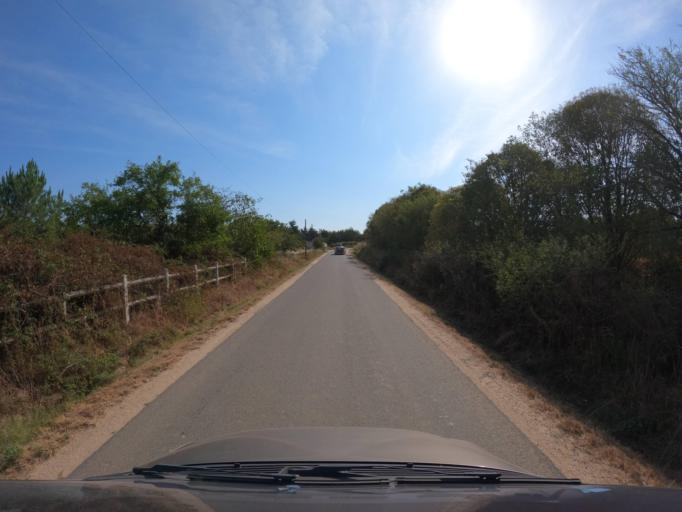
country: FR
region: Pays de la Loire
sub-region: Departement de la Vendee
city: Commequiers
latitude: 46.8126
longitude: -1.8300
